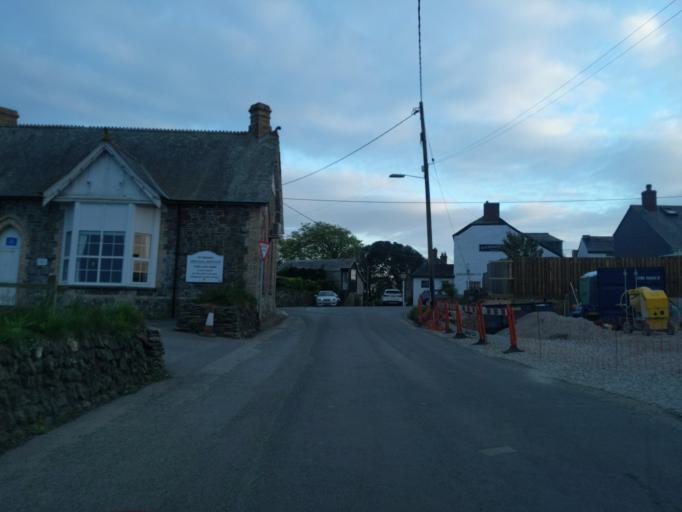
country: GB
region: England
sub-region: Cornwall
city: Polzeath
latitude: 50.5590
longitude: -4.8730
